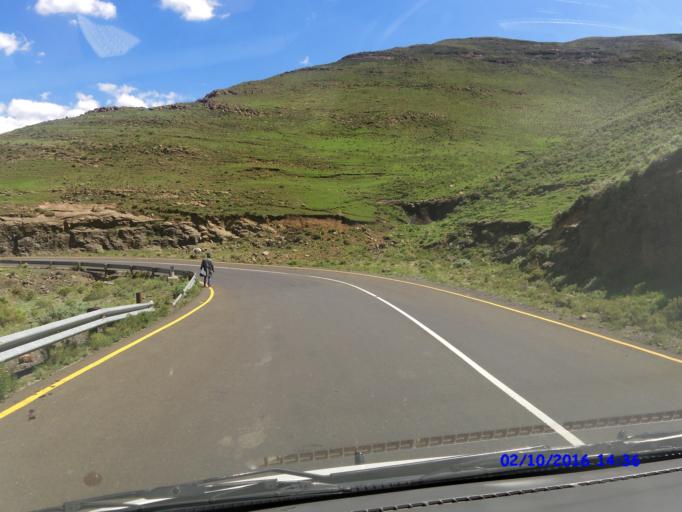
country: LS
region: Maseru
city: Nako
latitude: -29.5000
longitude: 28.0611
